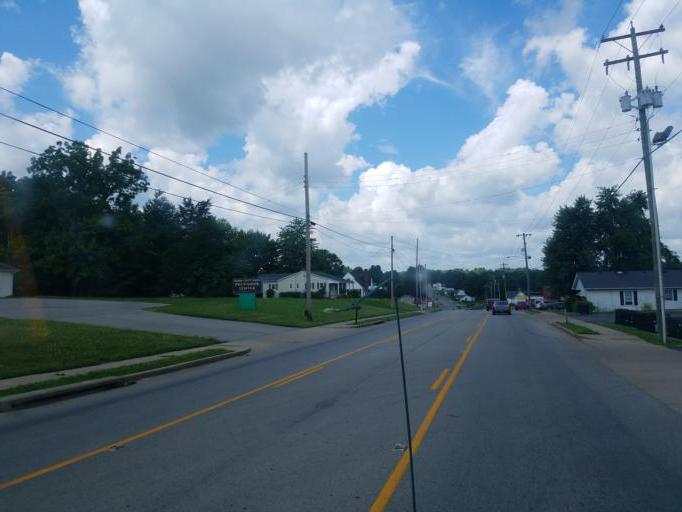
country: US
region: Kentucky
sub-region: Grayson County
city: Leitchfield
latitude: 37.4842
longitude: -86.2848
